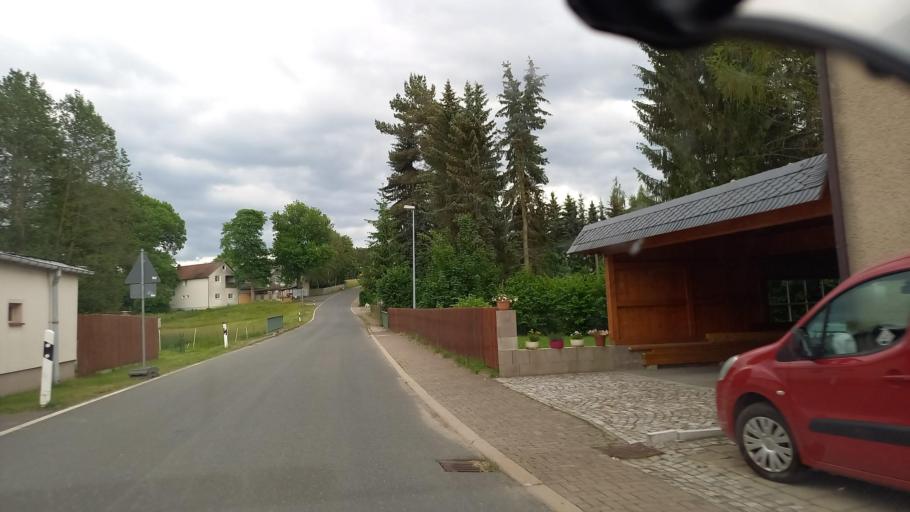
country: DE
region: Saxony
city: Waldkirchen
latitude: 50.6265
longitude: 12.3949
